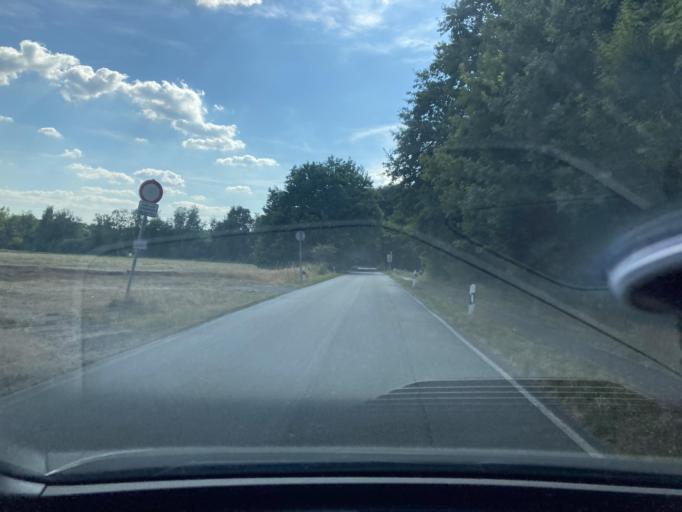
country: DE
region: Hesse
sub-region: Regierungsbezirk Darmstadt
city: Hanau am Main
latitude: 50.1042
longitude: 8.8921
